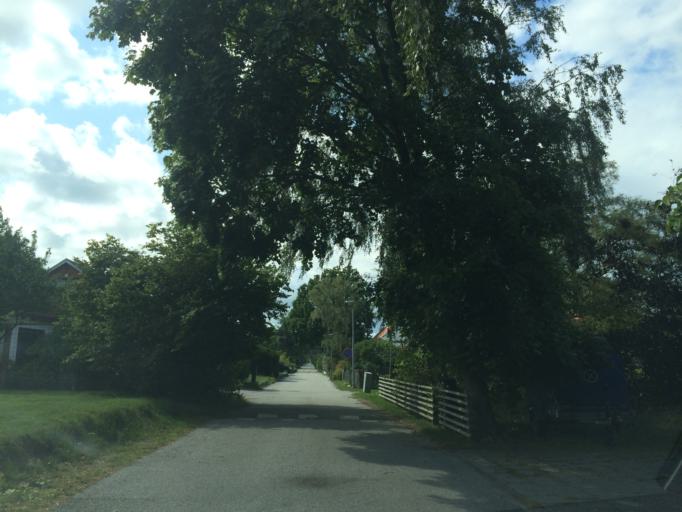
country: SE
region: Skane
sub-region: Vellinge Kommun
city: Skanor med Falsterbo
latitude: 55.3967
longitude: 12.8547
